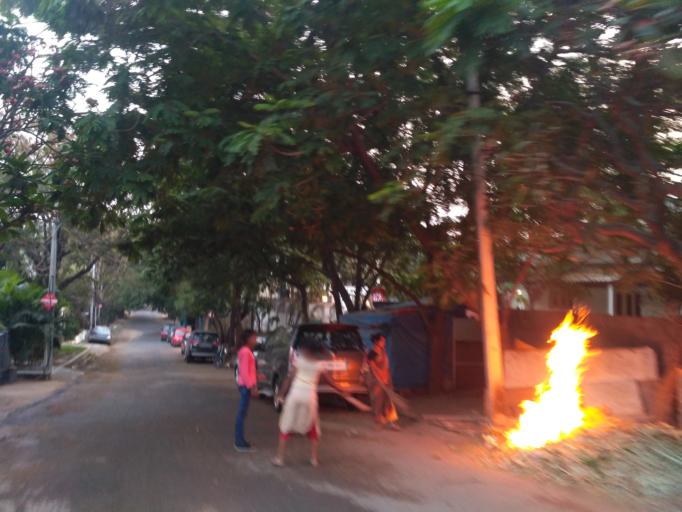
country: IN
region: Telangana
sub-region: Rangareddi
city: Kukatpalli
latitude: 17.4372
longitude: 78.4049
